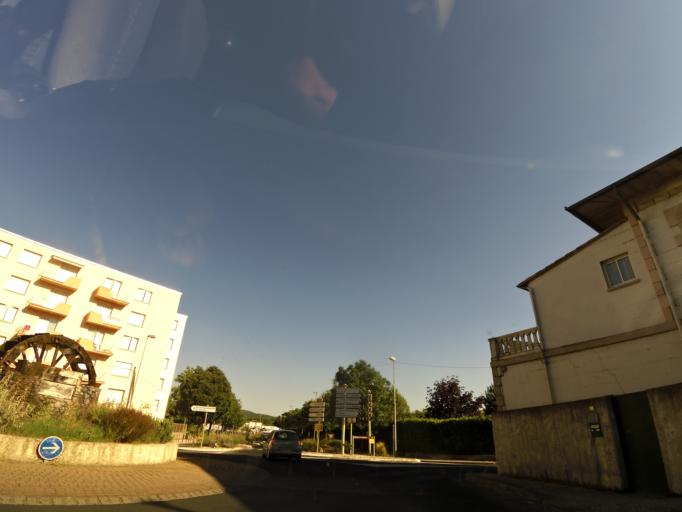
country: FR
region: Languedoc-Roussillon
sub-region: Departement de l'Herault
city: Ganges
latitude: 43.9317
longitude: 3.7042
